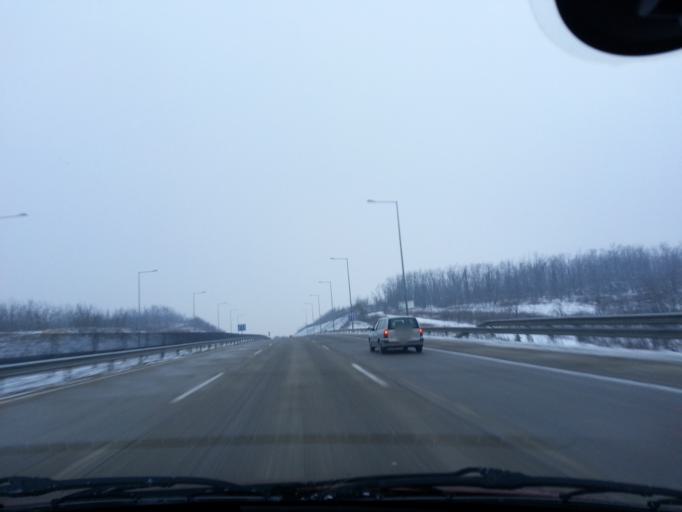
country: HU
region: Pest
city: Kerepes
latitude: 47.5660
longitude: 19.3234
